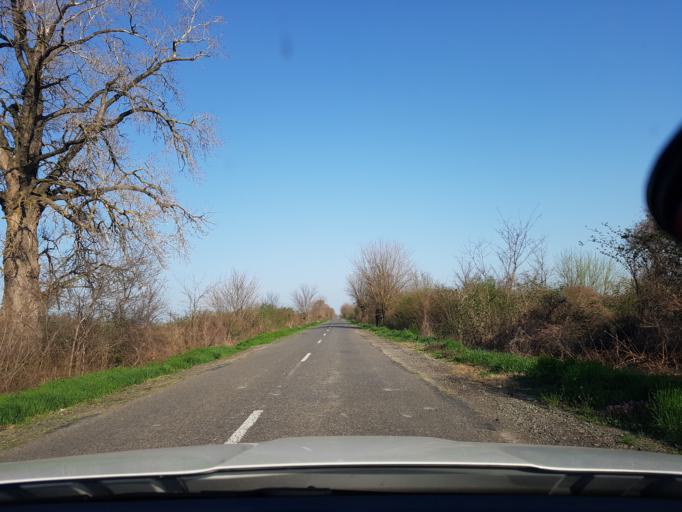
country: HU
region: Tolna
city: Ocseny
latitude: 46.3351
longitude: 18.8006
